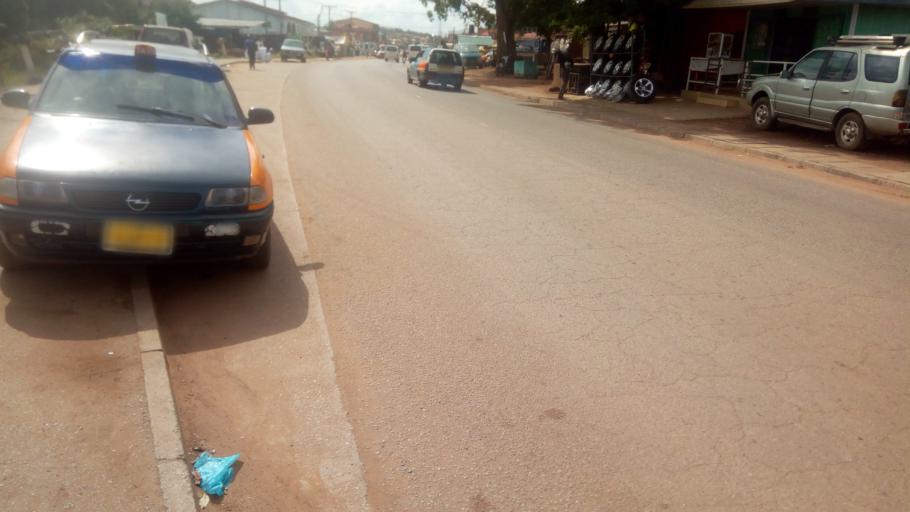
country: GH
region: Ashanti
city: Obuasi
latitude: 6.2063
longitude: -1.6826
